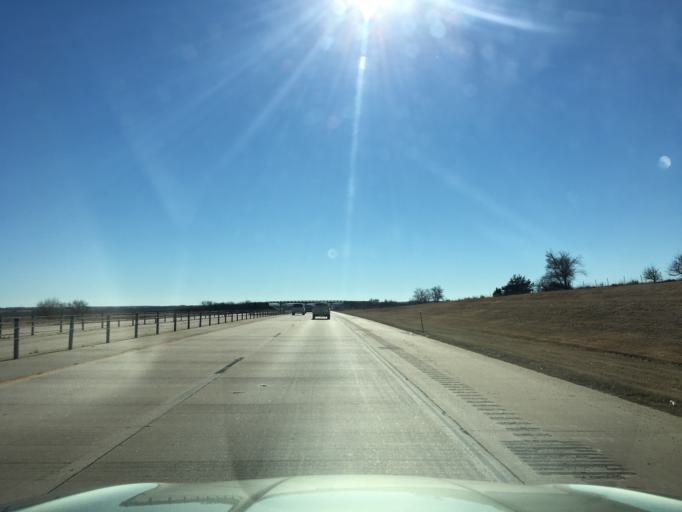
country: US
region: Oklahoma
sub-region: Noble County
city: Perry
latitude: 36.4528
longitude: -97.3271
